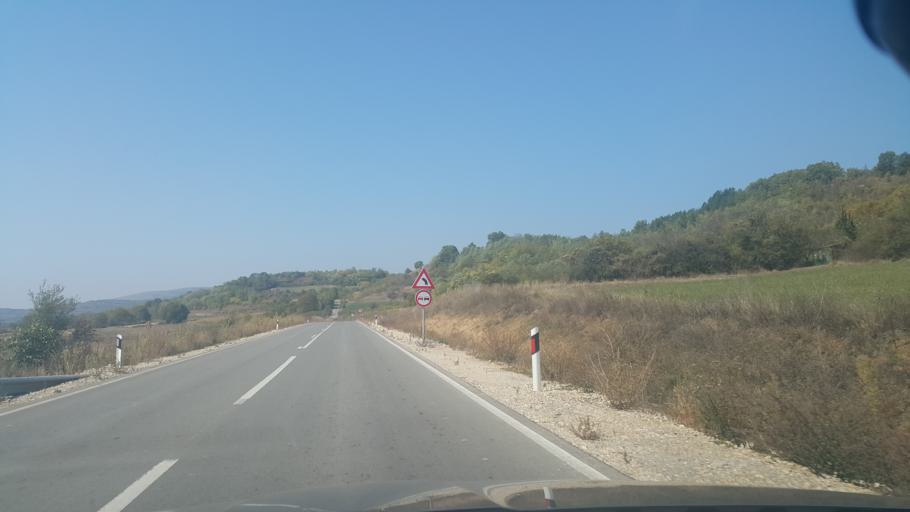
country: RS
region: Central Serbia
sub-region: Pirotski Okrug
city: Pirot
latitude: 43.2265
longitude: 22.4784
